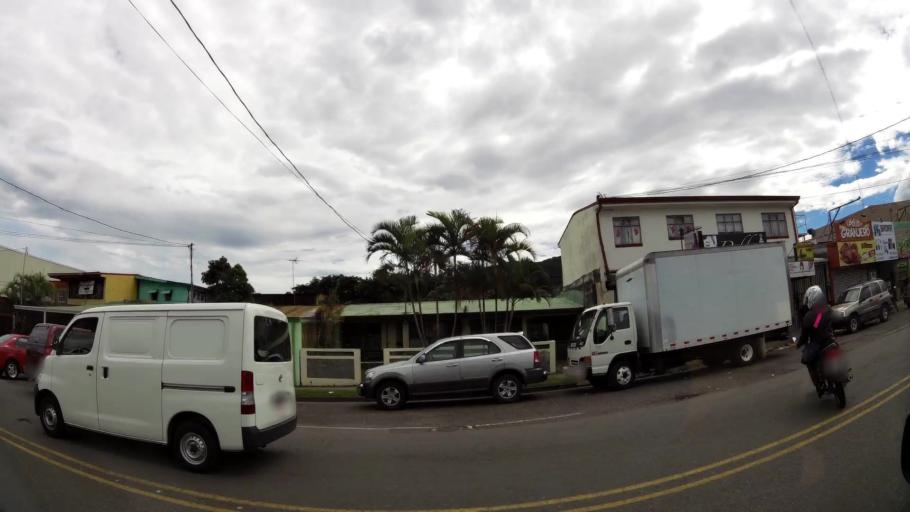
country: CR
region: San Jose
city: San Miguel
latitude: 9.8928
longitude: -84.0579
